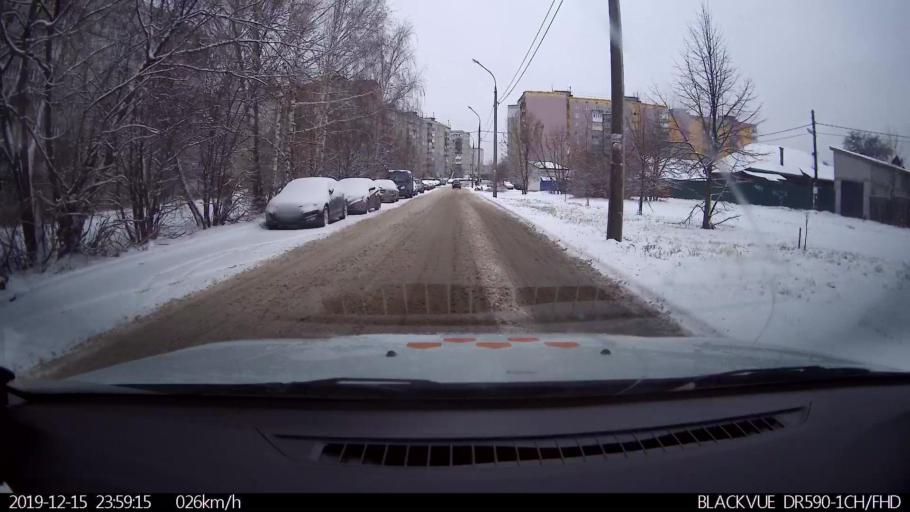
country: RU
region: Nizjnij Novgorod
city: Neklyudovo
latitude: 56.3638
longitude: 43.8532
